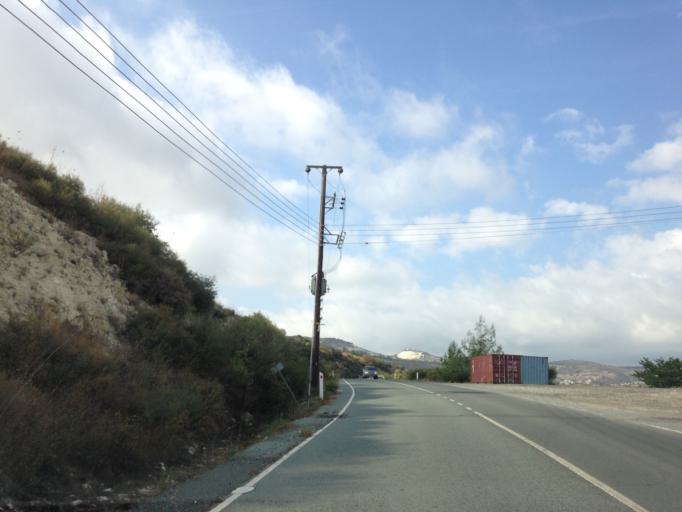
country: CY
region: Limassol
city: Pachna
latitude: 34.8378
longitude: 32.8091
